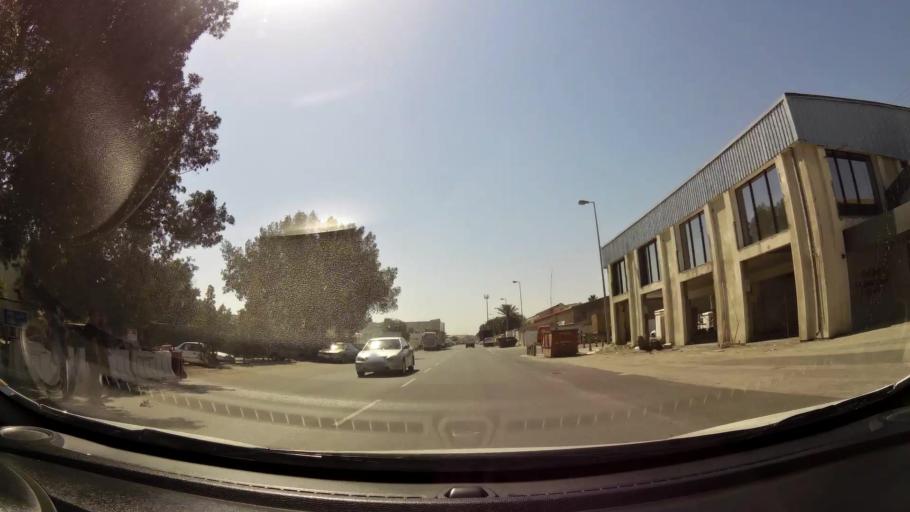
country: BH
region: Manama
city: Manama
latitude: 26.1986
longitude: 50.5977
